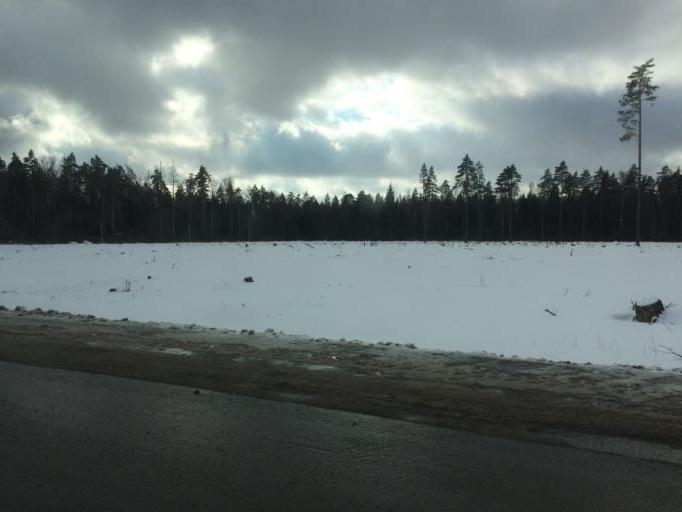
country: RU
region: Moskovskaya
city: Petrovo-Dal'neye
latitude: 55.7926
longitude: 37.1501
